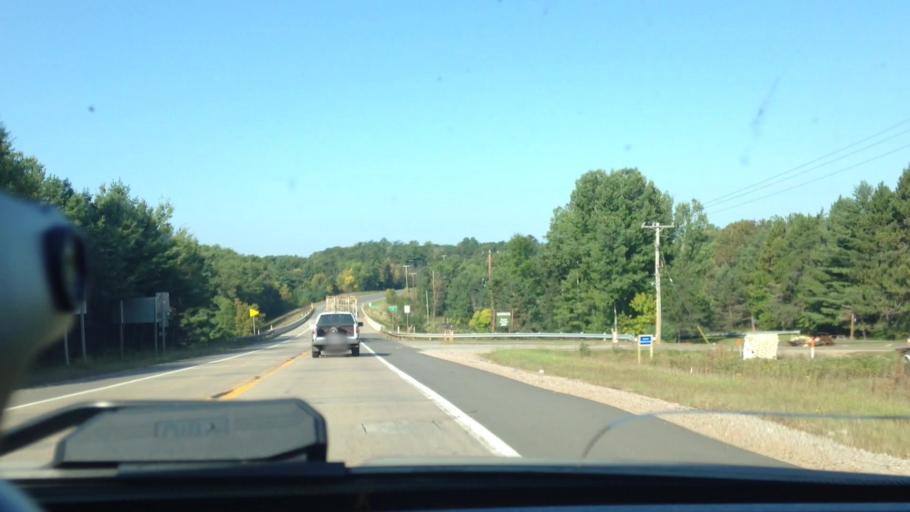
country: US
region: Michigan
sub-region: Dickinson County
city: Iron Mountain
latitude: 45.8662
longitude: -88.0721
